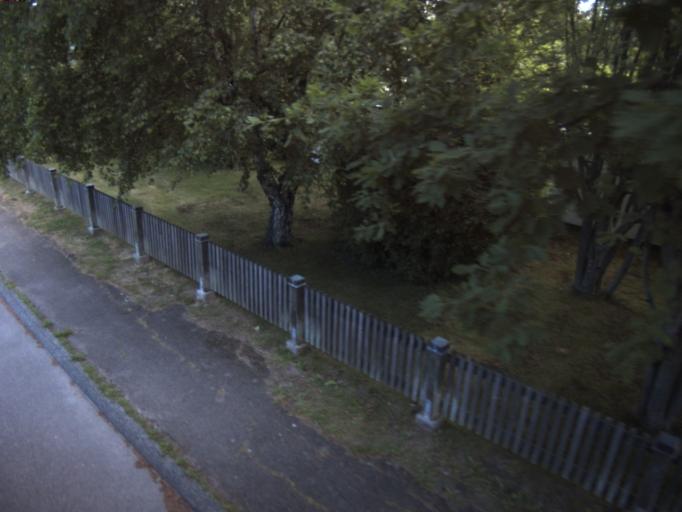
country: SE
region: Skane
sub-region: Helsingborg
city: Helsingborg
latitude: 56.0889
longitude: 12.6529
